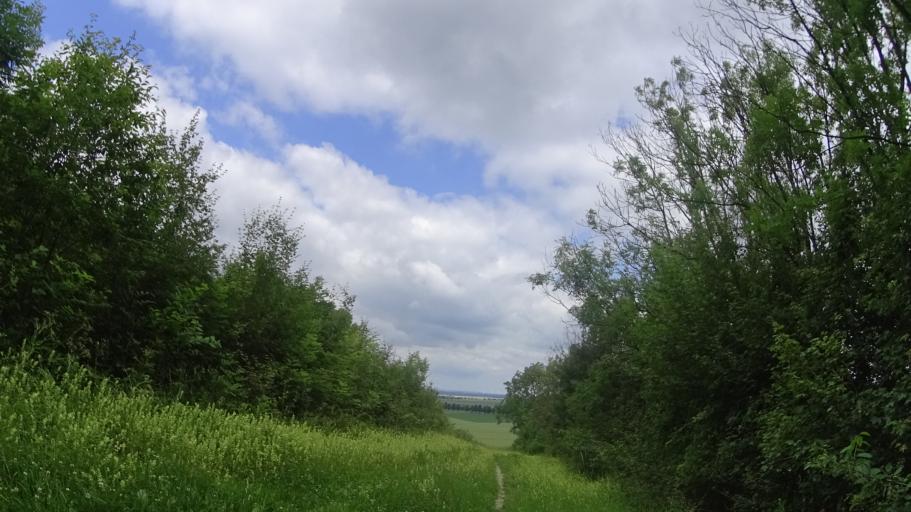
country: DE
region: Lower Saxony
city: Giesen
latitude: 52.1519
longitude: 9.8992
